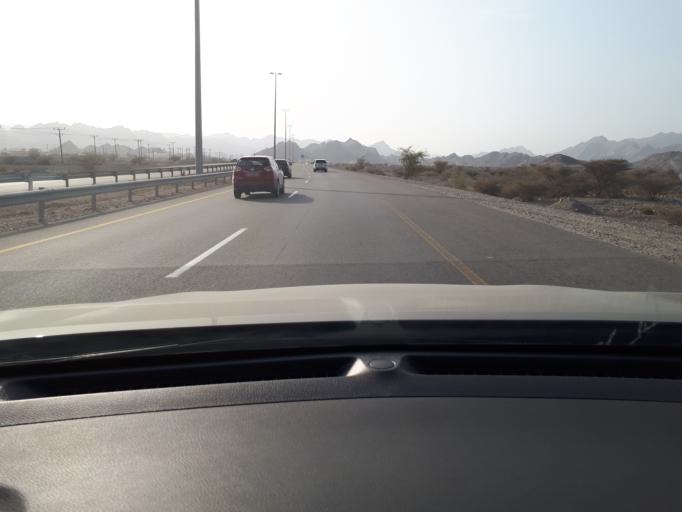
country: OM
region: Muhafazat Masqat
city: Muscat
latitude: 23.3007
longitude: 58.7387
